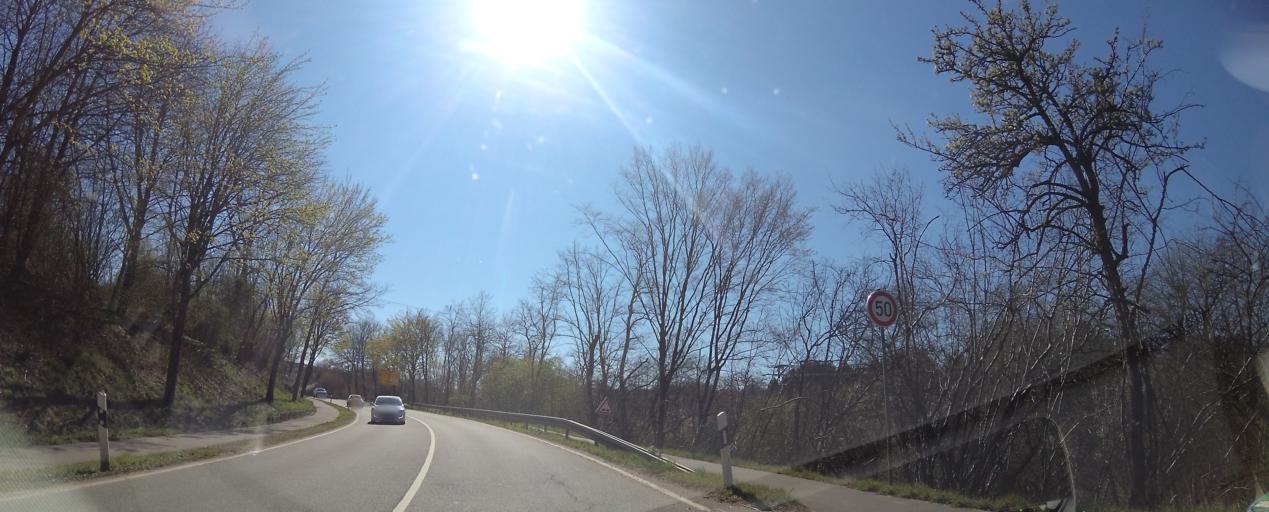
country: DE
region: Saarland
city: Riegelsberg
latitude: 49.3200
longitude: 6.9166
